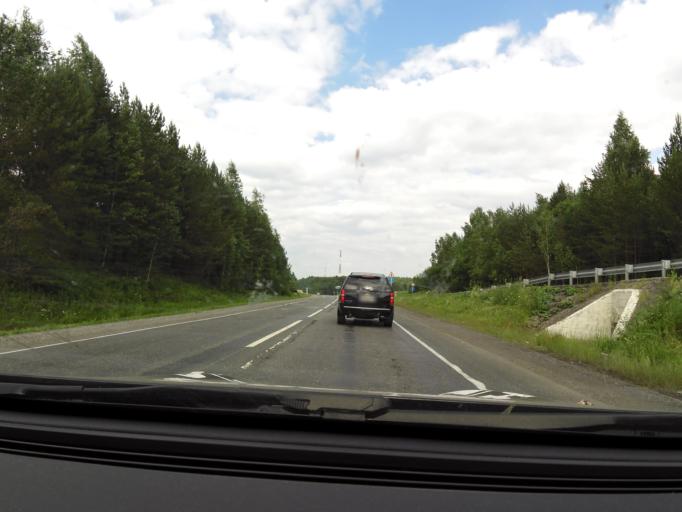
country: RU
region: Sverdlovsk
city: Druzhinino
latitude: 56.7993
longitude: 59.4659
